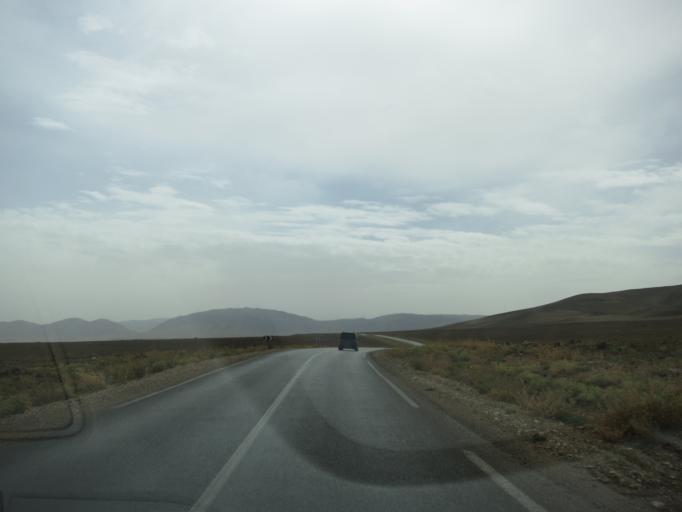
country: MA
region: Meknes-Tafilalet
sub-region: Ifrane
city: Azrou
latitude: 33.3013
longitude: -5.0980
